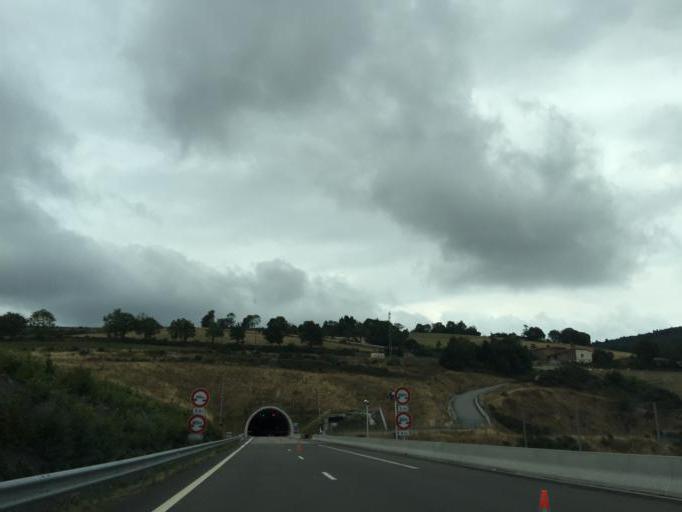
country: FR
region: Rhone-Alpes
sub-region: Departement de la Loire
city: Violay
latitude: 45.8599
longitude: 4.3250
